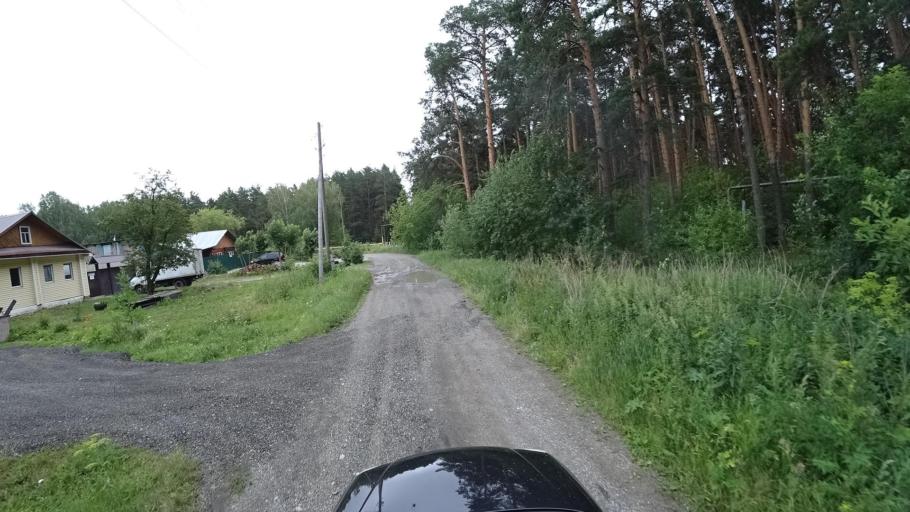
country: RU
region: Sverdlovsk
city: Kamyshlov
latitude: 56.8422
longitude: 62.7520
